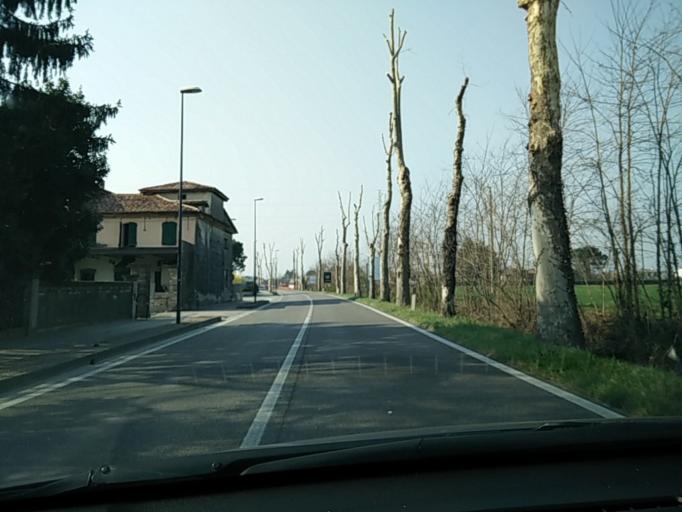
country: IT
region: Veneto
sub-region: Provincia di Treviso
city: Postioma
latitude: 45.7136
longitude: 12.1610
